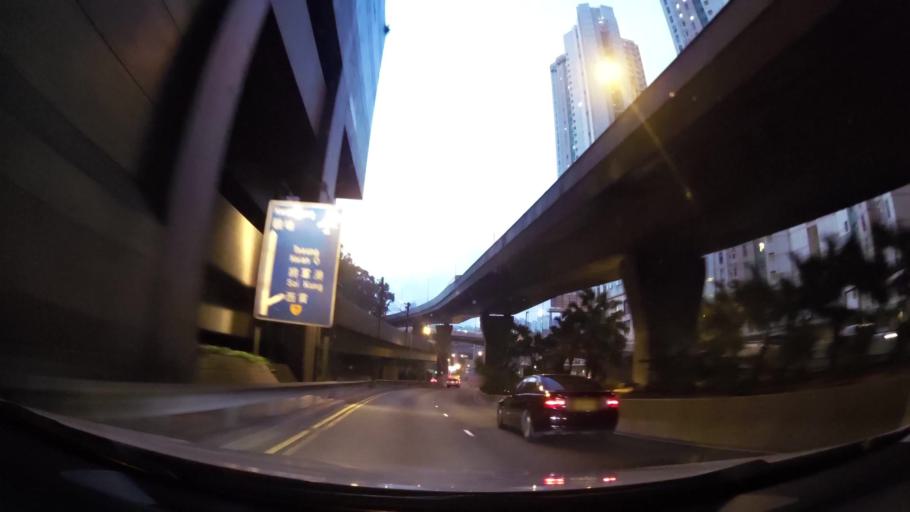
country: HK
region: Kowloon City
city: Kowloon
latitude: 22.3077
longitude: 114.2324
